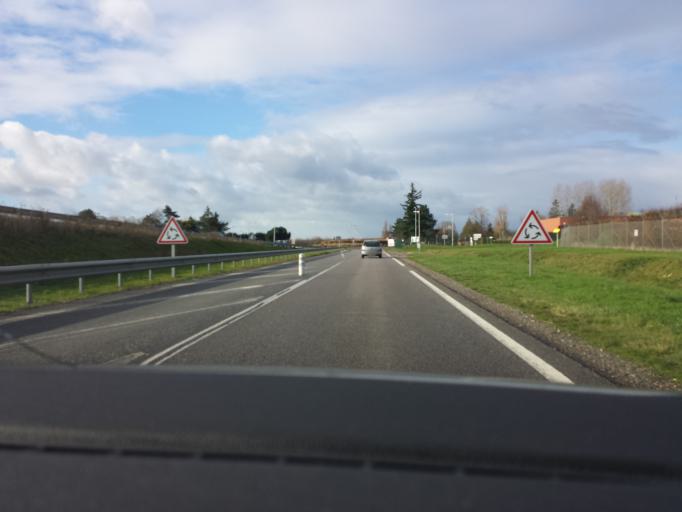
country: FR
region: Haute-Normandie
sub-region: Departement de l'Eure
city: Gravigny
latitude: 49.0152
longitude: 1.1968
